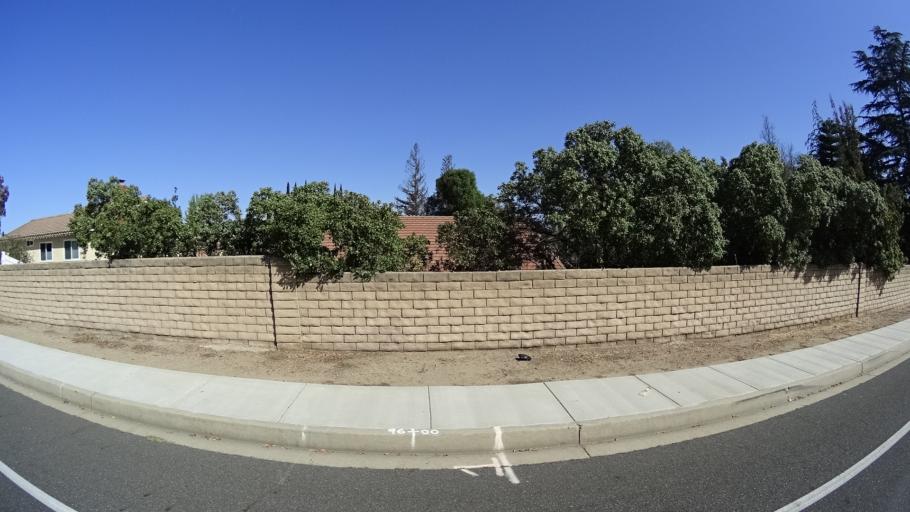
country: US
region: California
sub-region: Ventura County
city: Casa Conejo
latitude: 34.1778
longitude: -118.8954
